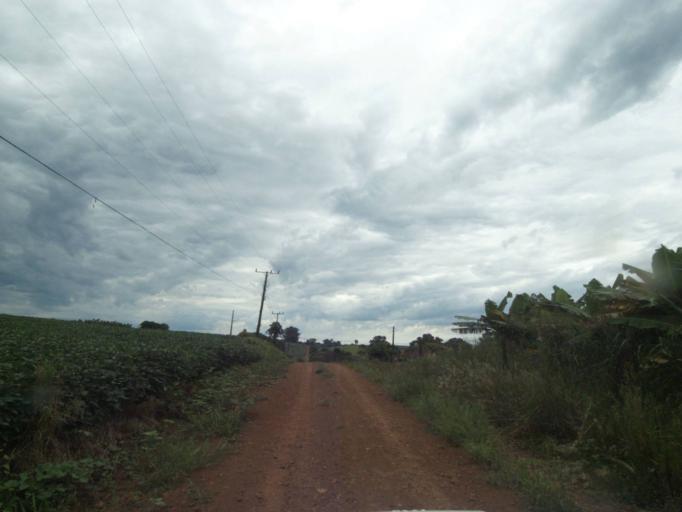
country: BR
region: Parana
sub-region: Guaraniacu
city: Guaraniacu
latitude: -24.9219
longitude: -52.9367
